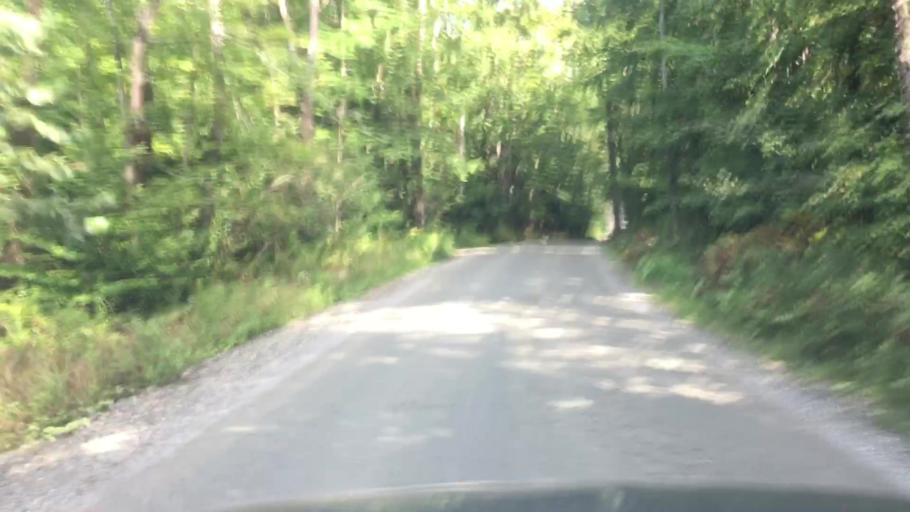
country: US
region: Vermont
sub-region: Windham County
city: Dover
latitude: 42.8220
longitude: -72.7804
